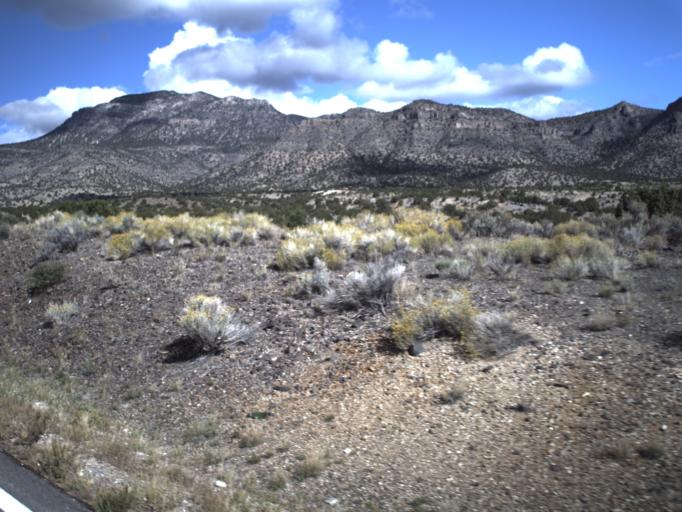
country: US
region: Utah
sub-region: Beaver County
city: Milford
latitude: 38.5073
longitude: -113.5163
